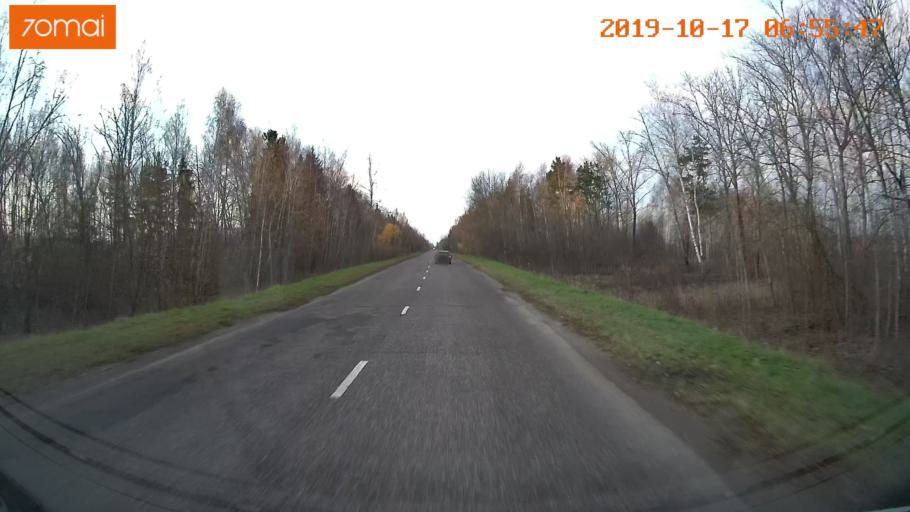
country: RU
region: Vladimir
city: Suzdal'
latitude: 56.4532
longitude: 40.4533
